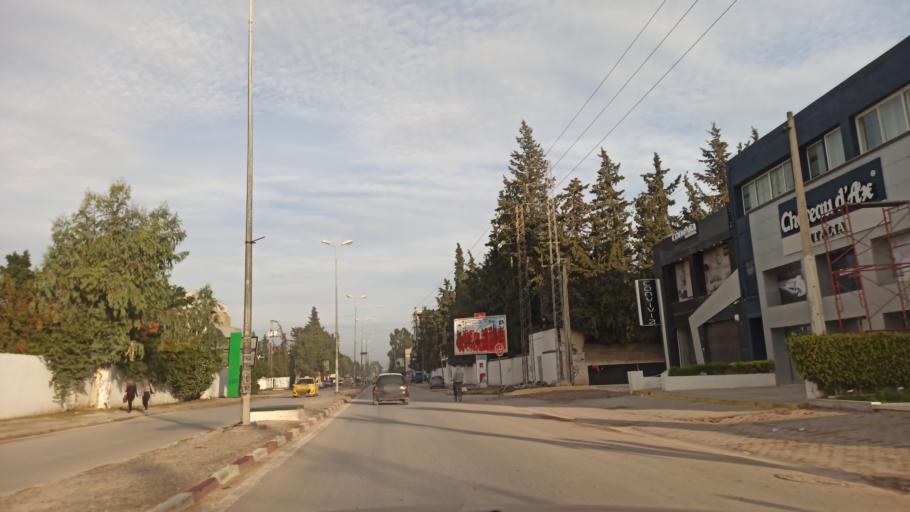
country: TN
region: Ariana
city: Ariana
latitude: 36.8682
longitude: 10.2502
